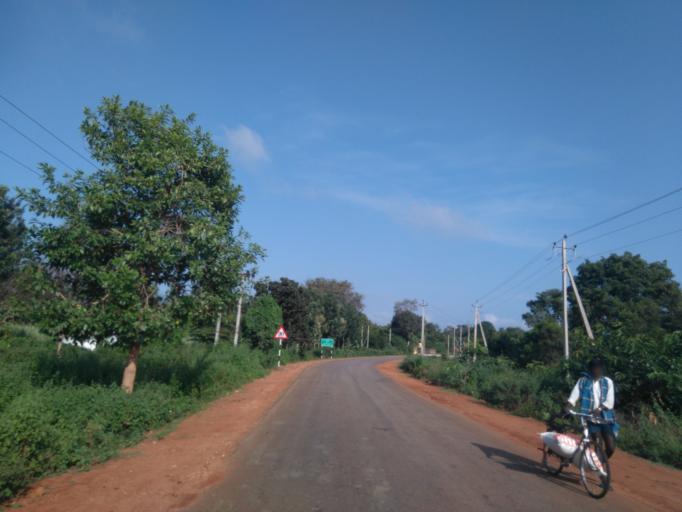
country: IN
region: Karnataka
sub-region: Chamrajnagar
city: Kollegal
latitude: 12.2605
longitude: 77.0436
